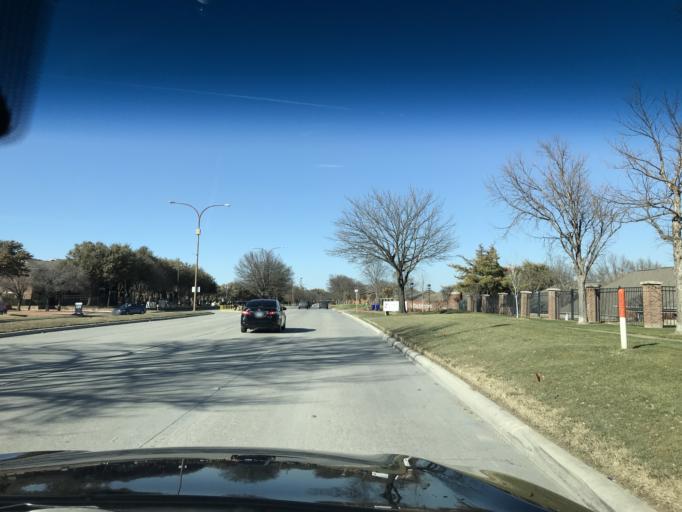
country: US
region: Texas
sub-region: Tarrant County
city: Benbrook
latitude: 32.6683
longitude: -97.4193
